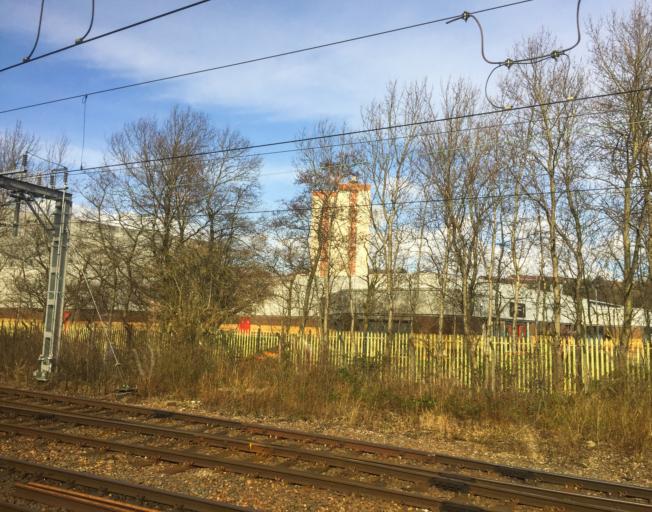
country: GB
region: Scotland
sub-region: East Dunbartonshire
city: Bishopbriggs
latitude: 55.8802
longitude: -4.2261
